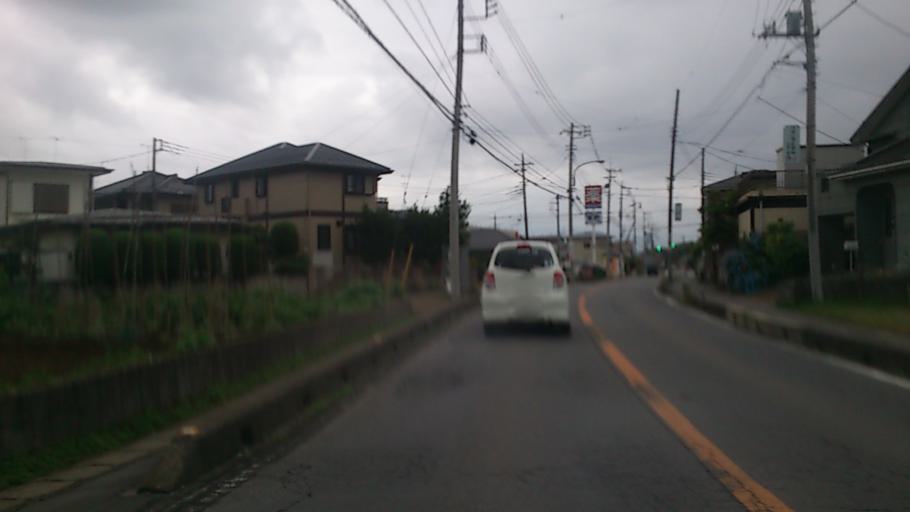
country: JP
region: Ibaraki
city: Ami
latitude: 36.0227
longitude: 140.2199
